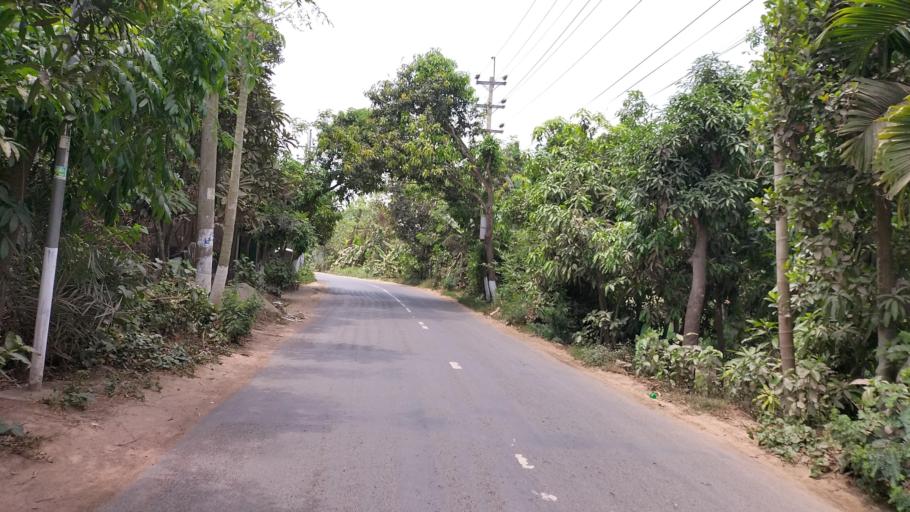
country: BD
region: Dhaka
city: Azimpur
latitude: 23.7311
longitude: 90.2988
